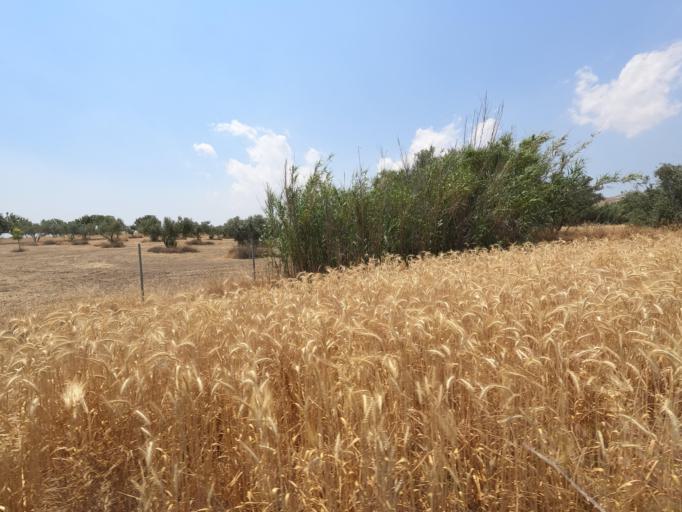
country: CY
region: Larnaka
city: Troulloi
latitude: 35.0346
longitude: 33.6057
